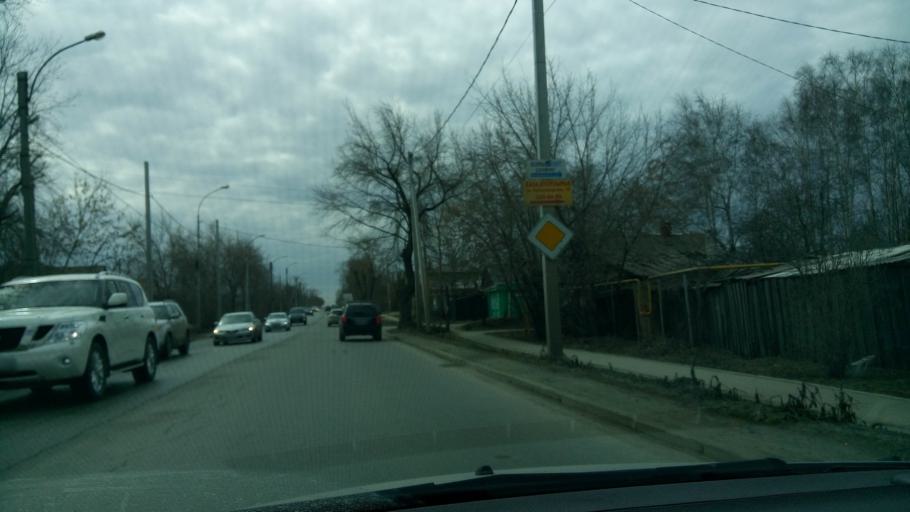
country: RU
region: Sverdlovsk
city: Yekaterinburg
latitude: 56.8715
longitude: 60.6837
